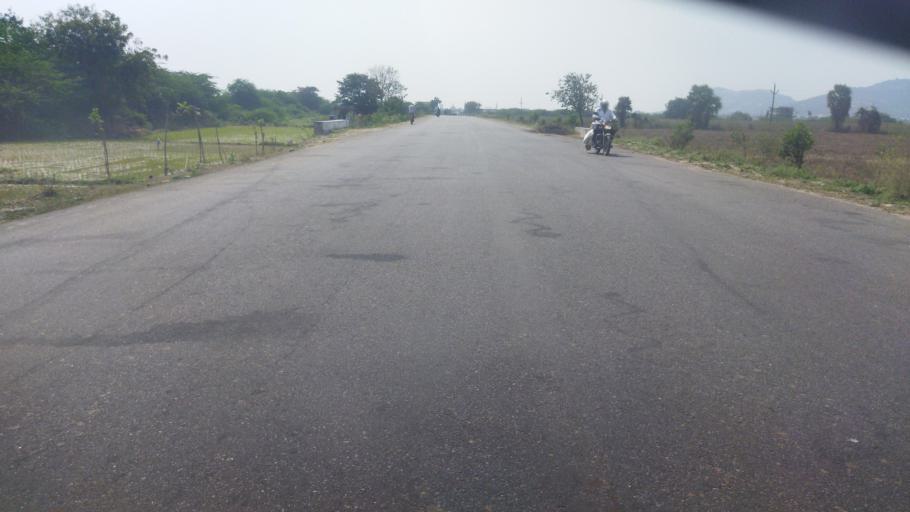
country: IN
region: Telangana
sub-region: Nalgonda
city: Nalgonda
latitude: 17.0831
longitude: 79.2842
